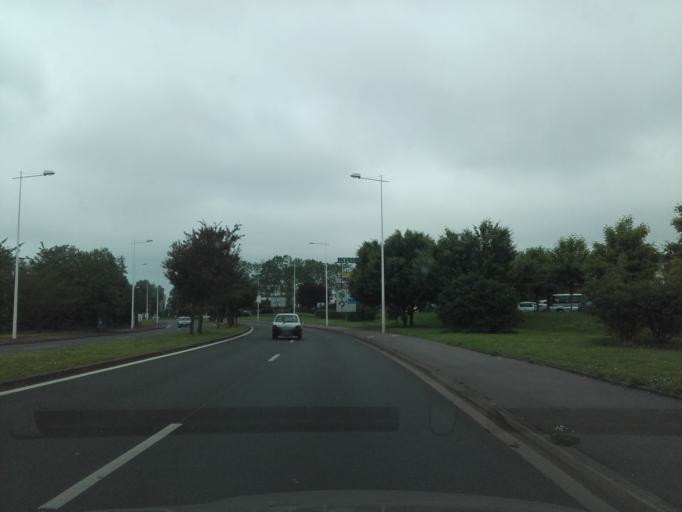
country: FR
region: Centre
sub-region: Departement d'Indre-et-Loire
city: Chanceaux-sur-Choisille
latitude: 47.4289
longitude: 0.7076
